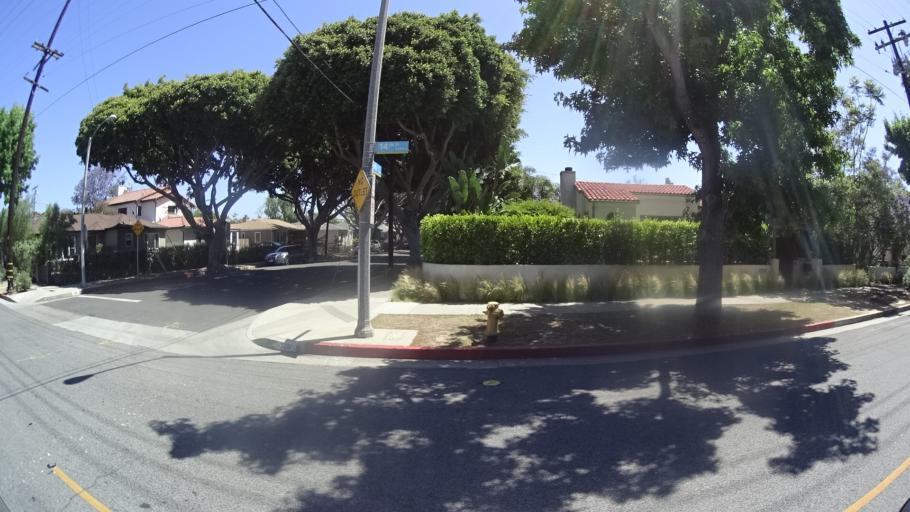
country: US
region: California
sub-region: Los Angeles County
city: Santa Monica
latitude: 34.0141
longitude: -118.4740
